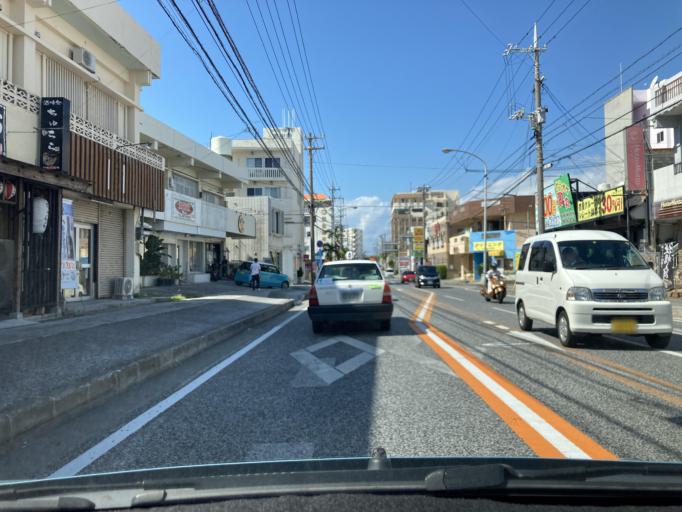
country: JP
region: Okinawa
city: Ginowan
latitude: 26.2614
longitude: 127.7427
